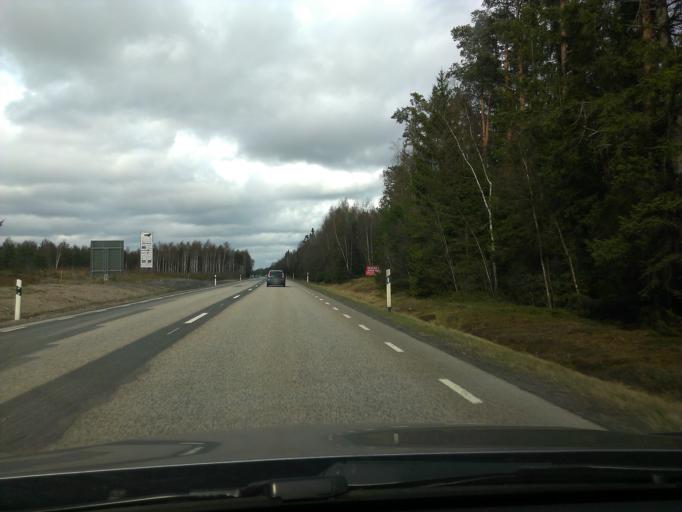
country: SE
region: Kronoberg
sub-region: Almhults Kommun
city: AElmhult
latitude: 56.5517
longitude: 14.1686
